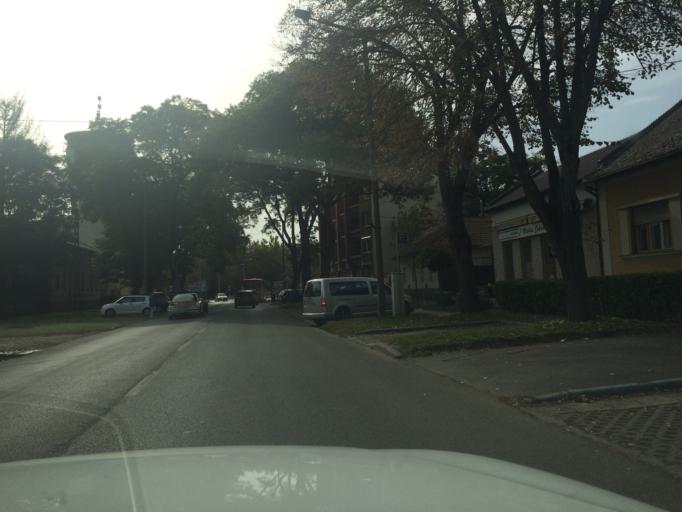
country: HU
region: Szabolcs-Szatmar-Bereg
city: Nyiregyhaza
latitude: 47.9493
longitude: 21.7157
